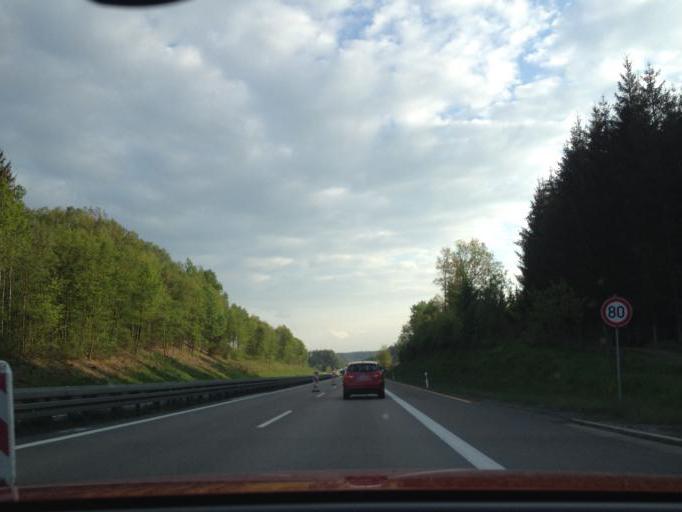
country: DE
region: Bavaria
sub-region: Upper Palatinate
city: Windischeschenbach
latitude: 49.7909
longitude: 12.1726
